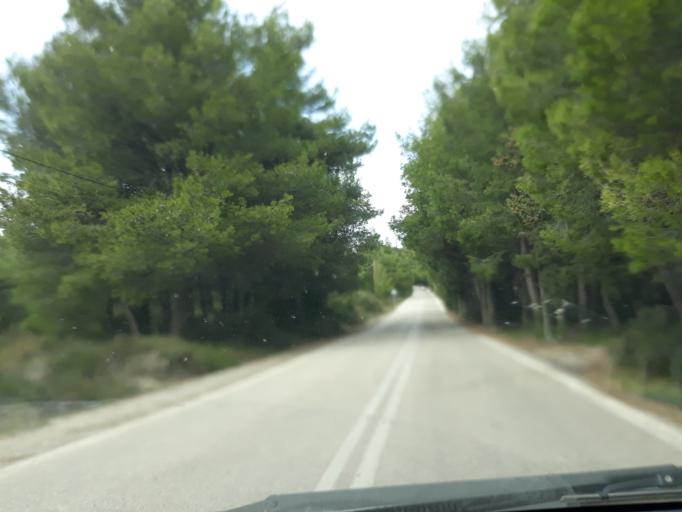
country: GR
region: Attica
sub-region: Nomarchia Anatolikis Attikis
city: Varybobi
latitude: 38.1390
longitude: 23.7930
